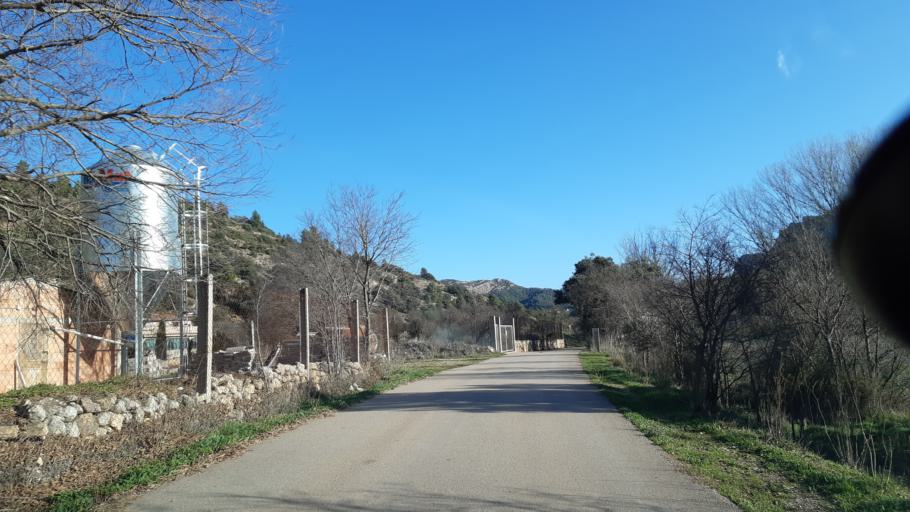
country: ES
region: Aragon
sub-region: Provincia de Teruel
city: Valderrobres
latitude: 40.8420
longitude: 0.2004
